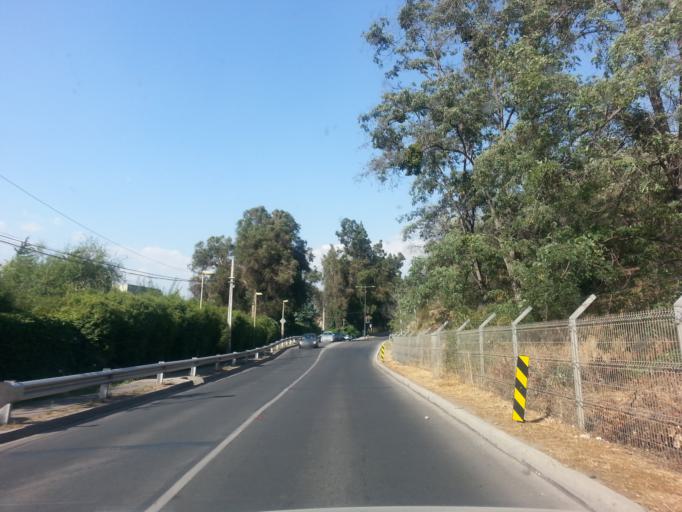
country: CL
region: Santiago Metropolitan
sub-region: Provincia de Santiago
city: Villa Presidente Frei, Nunoa, Santiago, Chile
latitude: -33.3818
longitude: -70.5135
